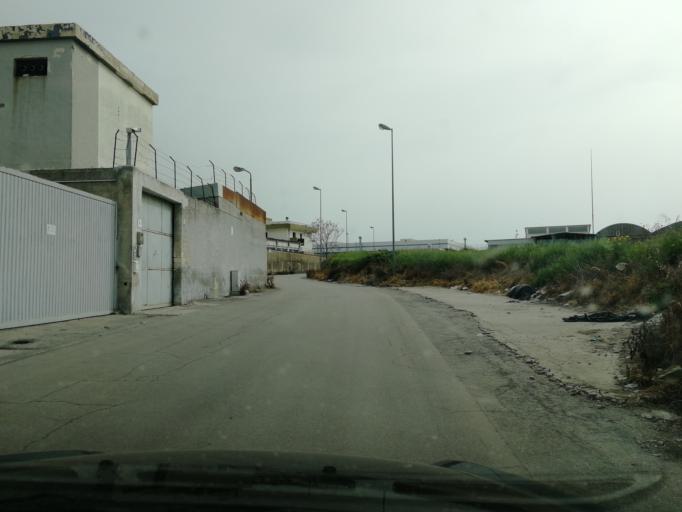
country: IT
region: Apulia
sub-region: Provincia di Barletta - Andria - Trani
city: Barletta
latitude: 41.3128
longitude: 16.3102
